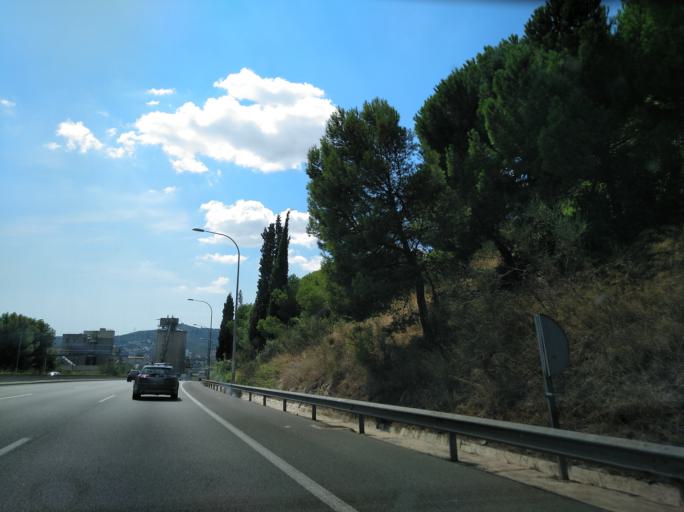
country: ES
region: Catalonia
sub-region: Provincia de Barcelona
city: Montcada i Reixac
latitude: 41.4771
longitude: 2.1837
